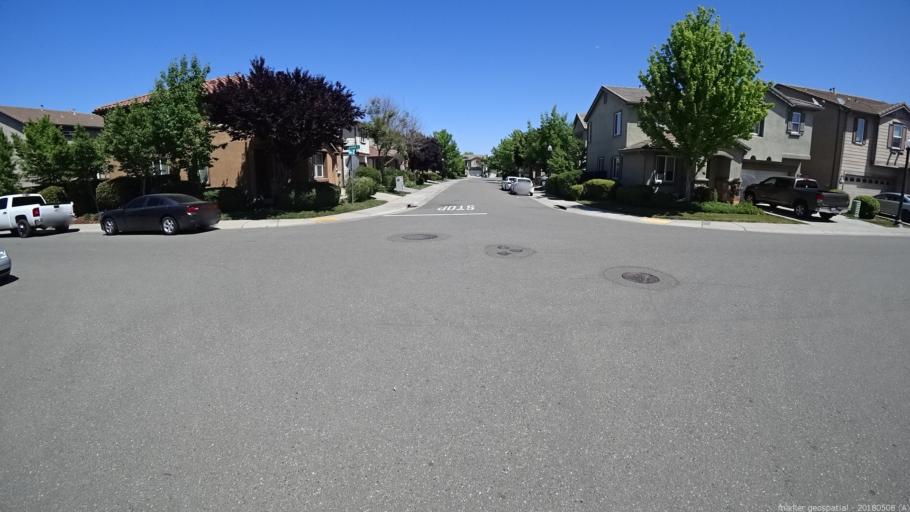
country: US
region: California
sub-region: Sacramento County
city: Elverta
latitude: 38.6770
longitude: -121.5387
